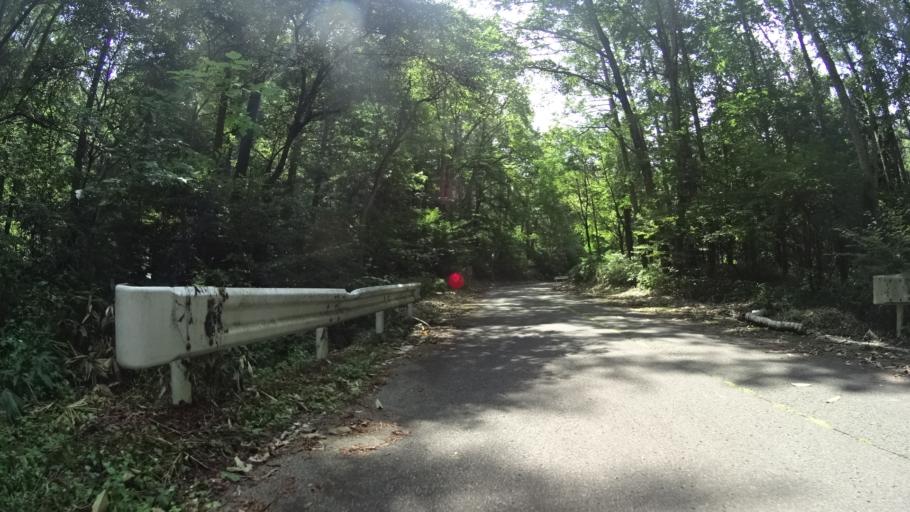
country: JP
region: Yamanashi
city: Nirasaki
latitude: 35.8828
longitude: 138.4799
